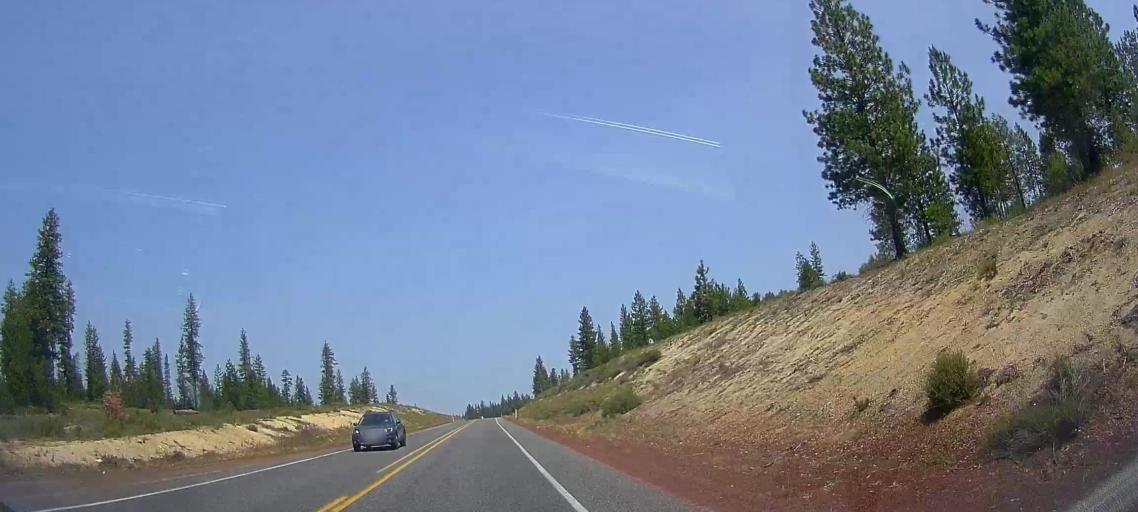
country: US
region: Oregon
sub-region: Deschutes County
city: La Pine
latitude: 43.4135
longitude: -121.7205
